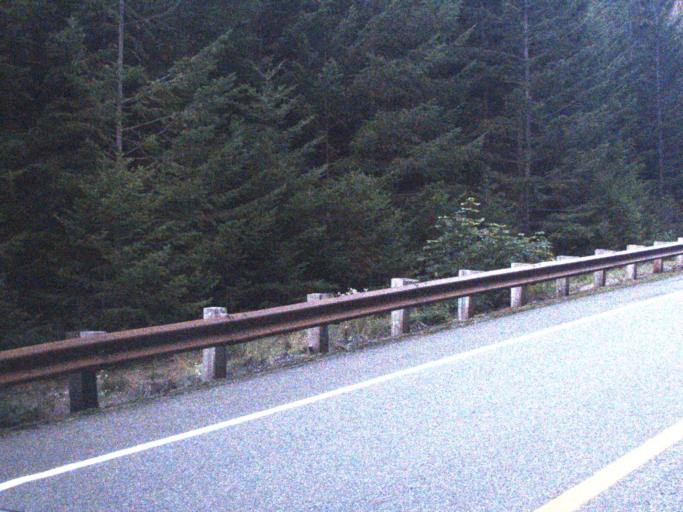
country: US
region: Washington
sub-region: Snohomish County
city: Darrington
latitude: 48.6832
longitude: -120.8839
